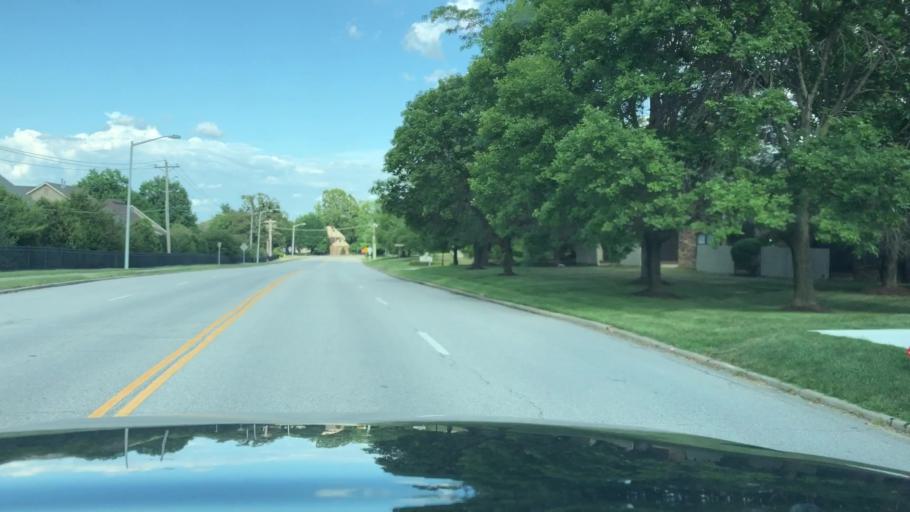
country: US
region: Missouri
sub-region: Saint Charles County
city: Lake Saint Louis
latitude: 38.7959
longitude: -90.8104
